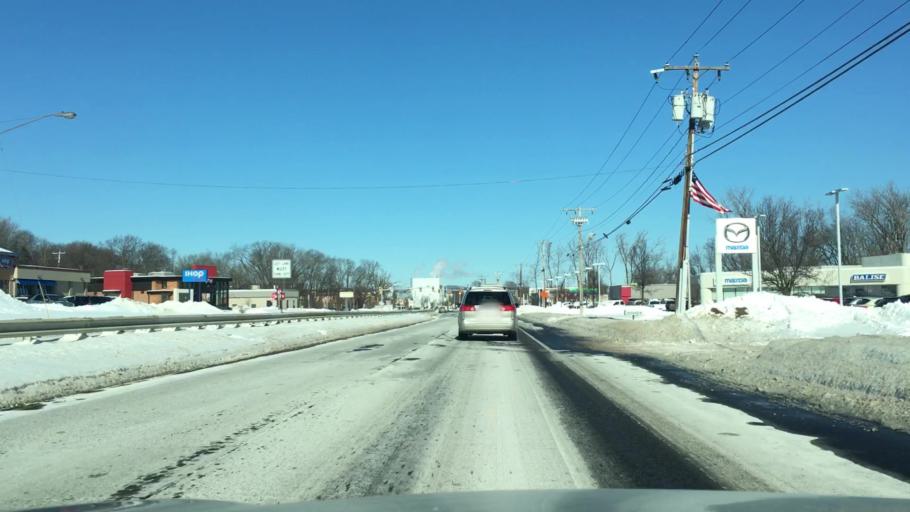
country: US
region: Massachusetts
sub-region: Hampden County
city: West Springfield
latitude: 42.1224
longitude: -72.6256
